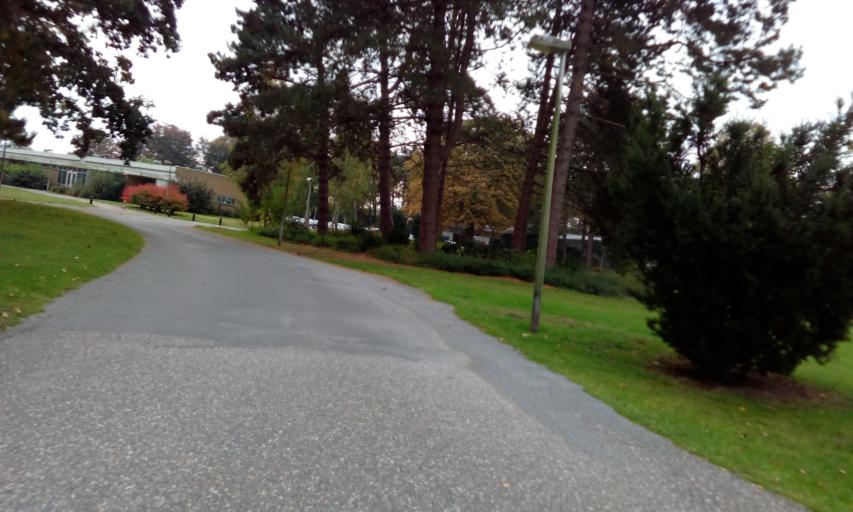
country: NL
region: South Holland
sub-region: Gemeente Oud-Beijerland
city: Oud-Beijerland
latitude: 51.8456
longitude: 4.3919
